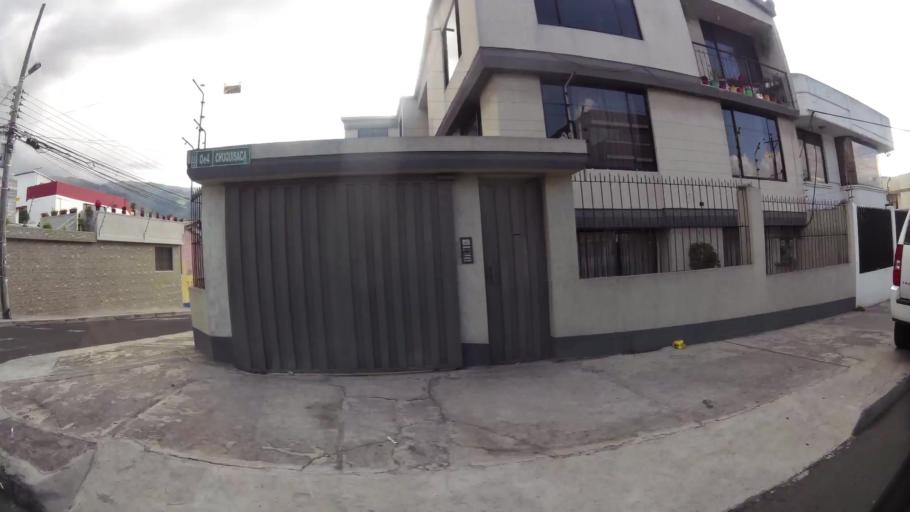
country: EC
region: Pichincha
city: Quito
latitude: -0.1180
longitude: -78.4888
